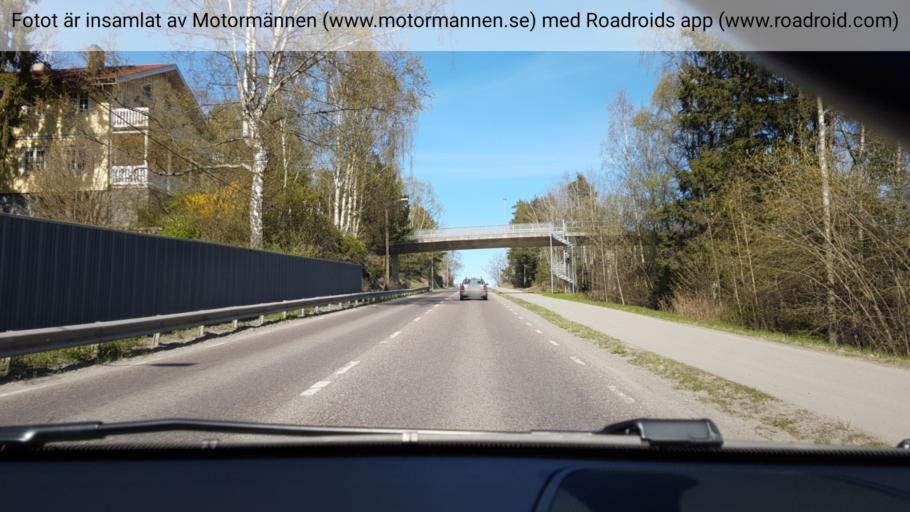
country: SE
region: Stockholm
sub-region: Botkyrka Kommun
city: Tullinge
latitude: 59.2077
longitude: 17.9106
